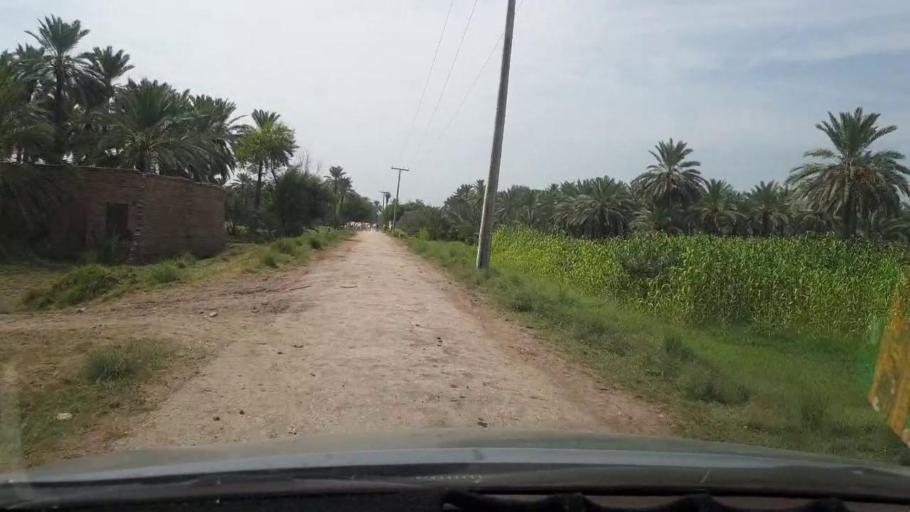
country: PK
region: Sindh
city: Khairpur
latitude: 27.4956
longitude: 68.7545
